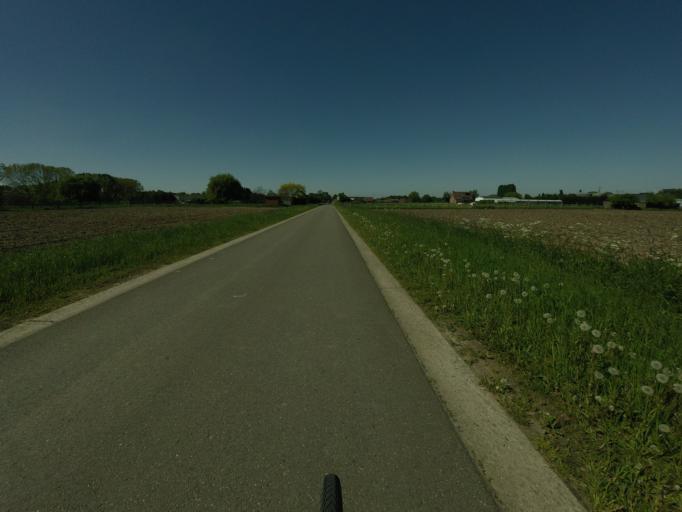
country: BE
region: Flanders
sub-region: Provincie Antwerpen
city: Borsbeek
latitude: 51.1812
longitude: 4.4976
